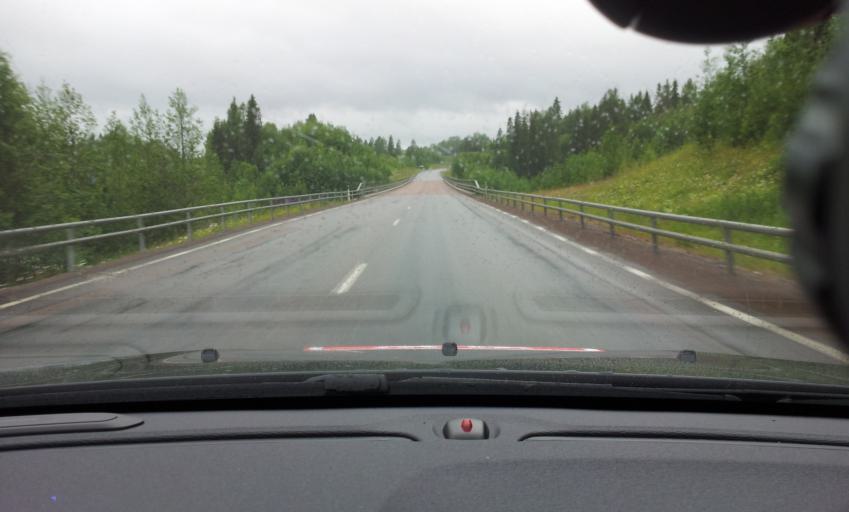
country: SE
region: Jaemtland
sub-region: Ragunda Kommun
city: Hammarstrand
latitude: 63.0317
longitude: 16.5994
